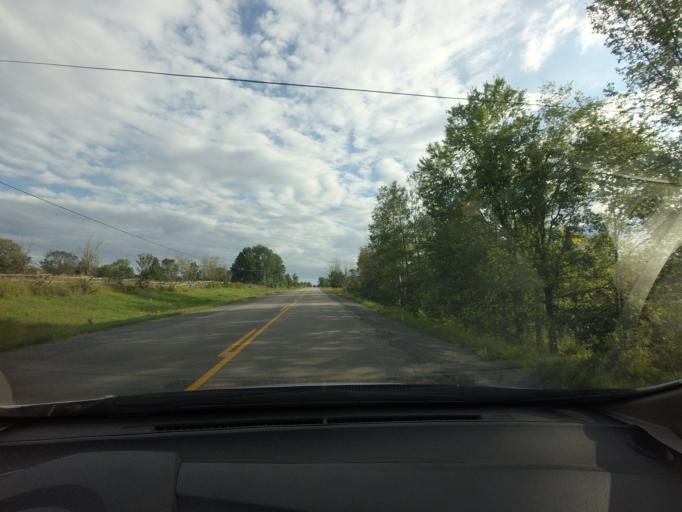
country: CA
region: Ontario
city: Perth
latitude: 44.7298
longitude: -76.3975
